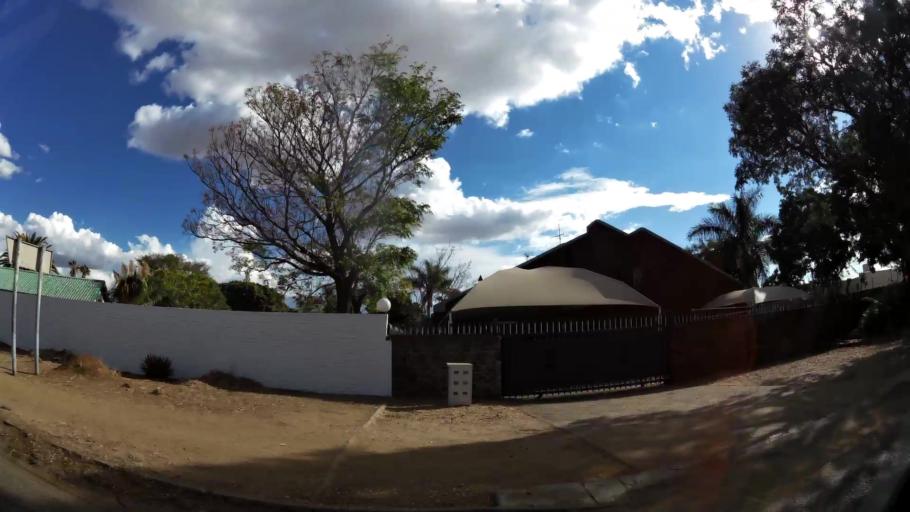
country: ZA
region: Limpopo
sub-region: Capricorn District Municipality
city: Polokwane
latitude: -23.9001
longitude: 29.4755
